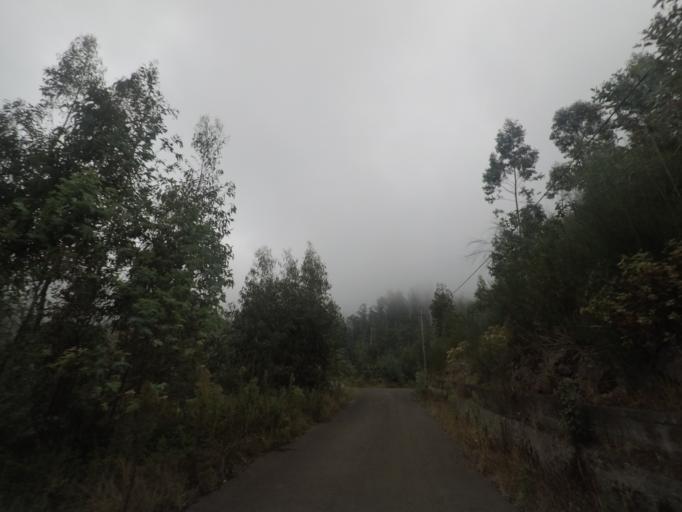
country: PT
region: Madeira
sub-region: Funchal
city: Nossa Senhora do Monte
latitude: 32.6934
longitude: -16.9085
